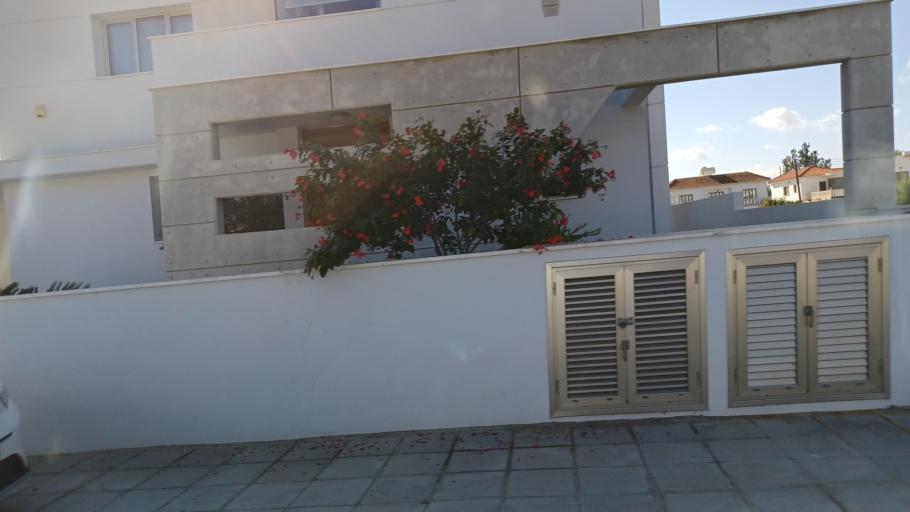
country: CY
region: Larnaka
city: Pyla
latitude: 34.9983
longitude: 33.6846
